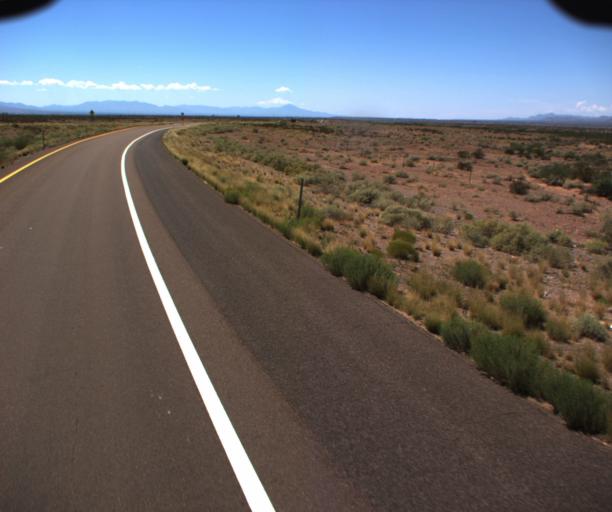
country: US
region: Arizona
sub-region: Graham County
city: Safford
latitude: 32.7926
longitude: -109.5504
